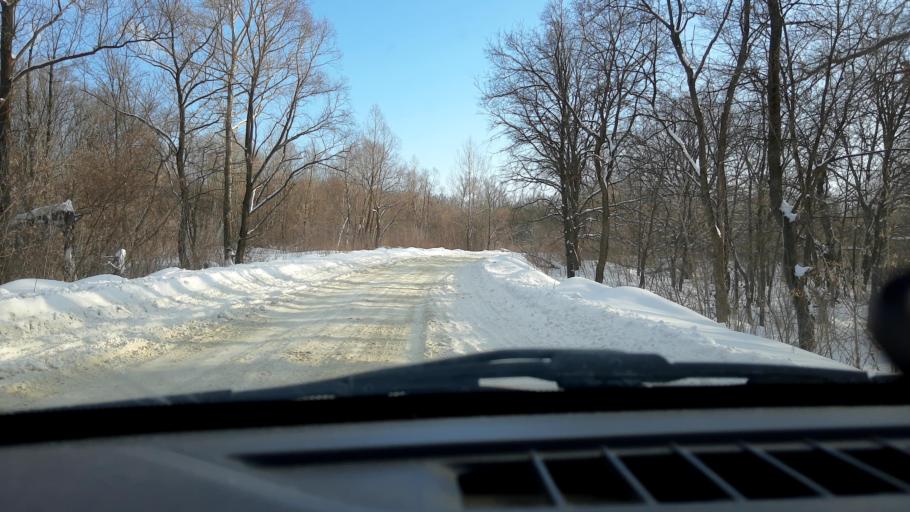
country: RU
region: Bashkortostan
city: Ufa
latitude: 54.6395
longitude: 56.0063
